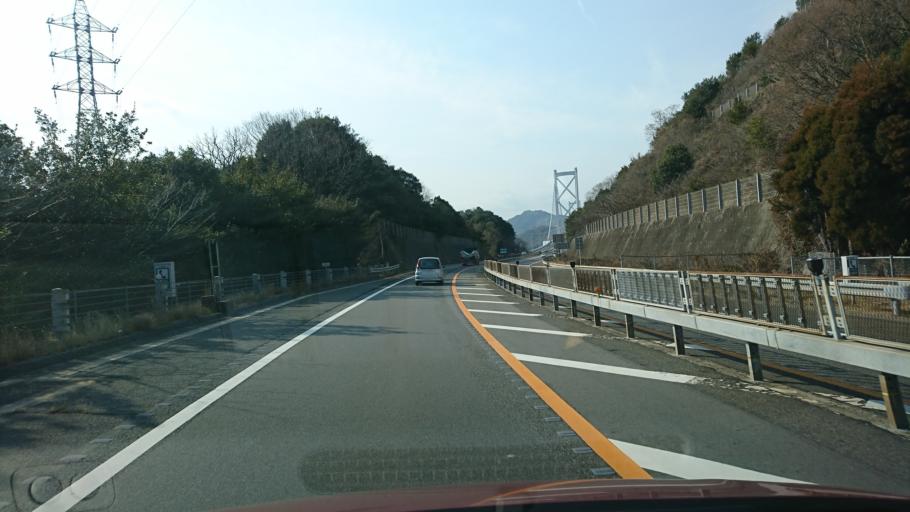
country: JP
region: Hiroshima
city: Onomichi
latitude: 34.3620
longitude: 133.1911
